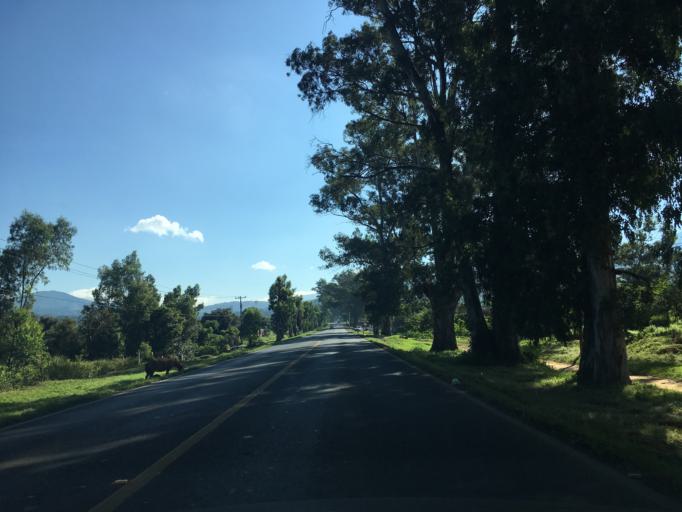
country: MX
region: Mexico
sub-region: Chalco
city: Zopoco
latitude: 19.8431
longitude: -102.0801
